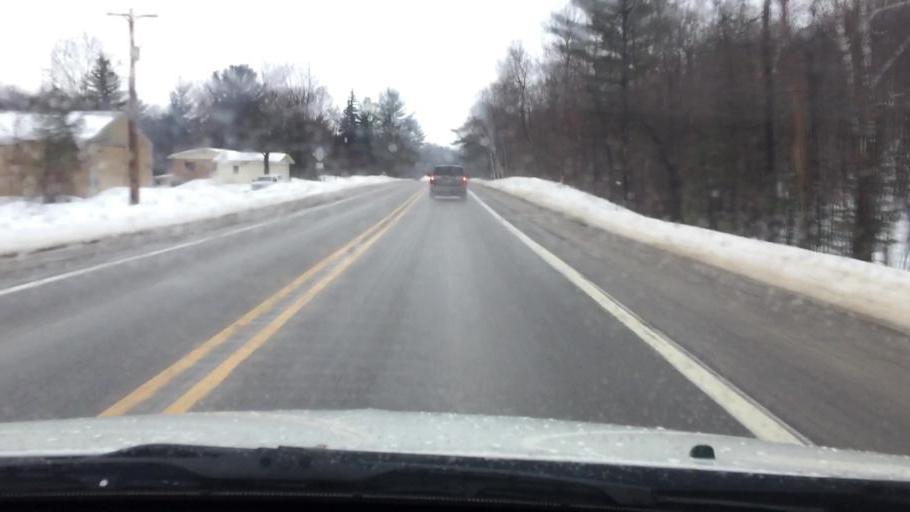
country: US
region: Michigan
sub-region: Charlevoix County
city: East Jordan
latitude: 45.2267
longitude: -85.1805
